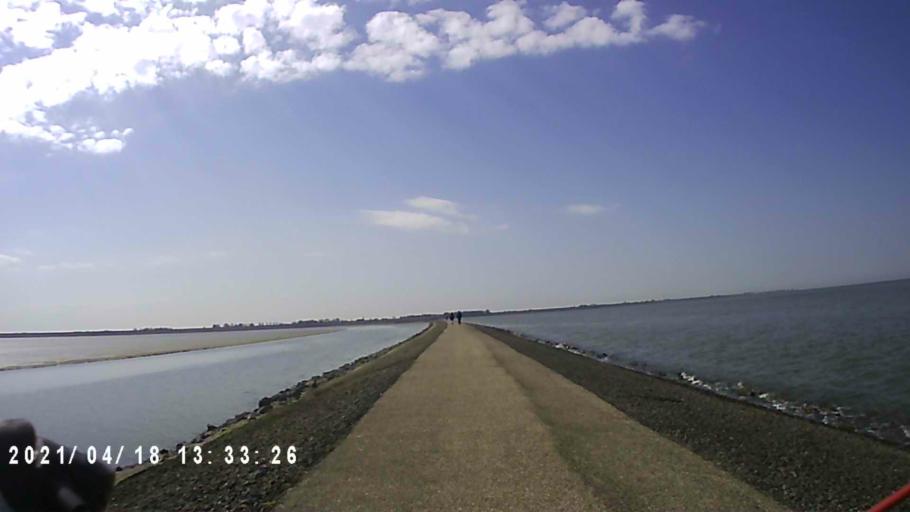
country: NL
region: Friesland
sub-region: Gemeente Dongeradeel
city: Anjum
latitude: 53.4137
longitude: 6.0983
